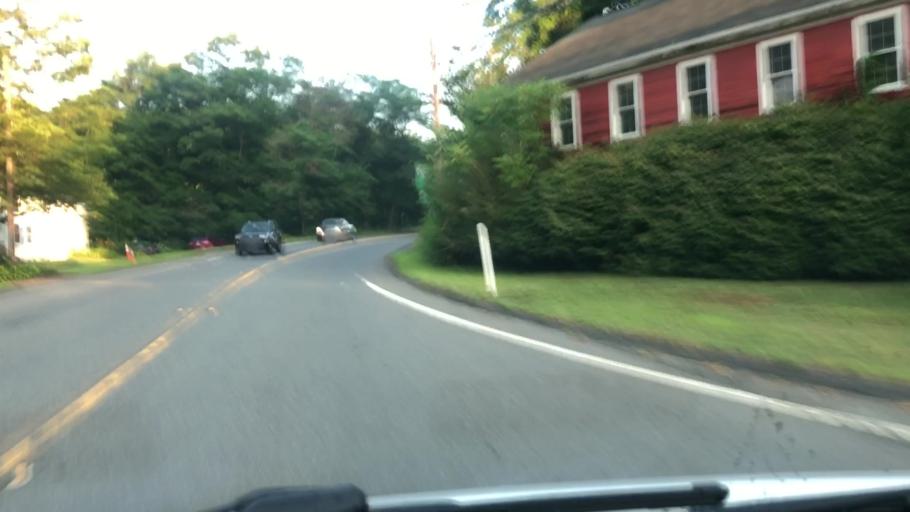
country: US
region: Massachusetts
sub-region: Hampshire County
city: Williamsburg
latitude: 42.3938
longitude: -72.7351
